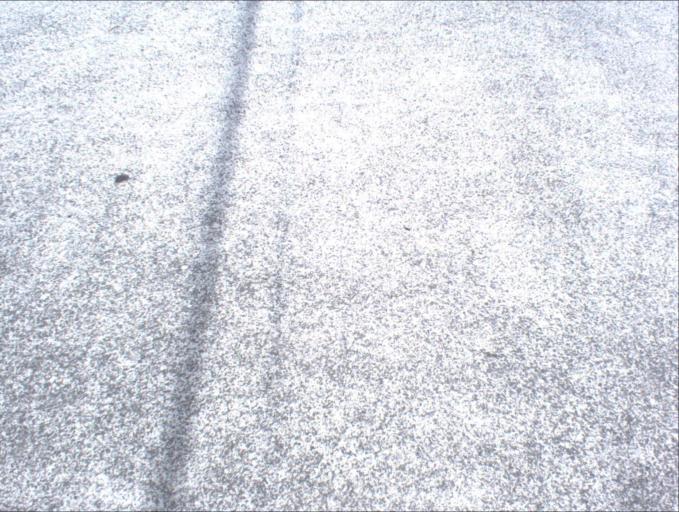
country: AU
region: Queensland
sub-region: Logan
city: Rochedale South
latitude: -27.5988
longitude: 153.1095
